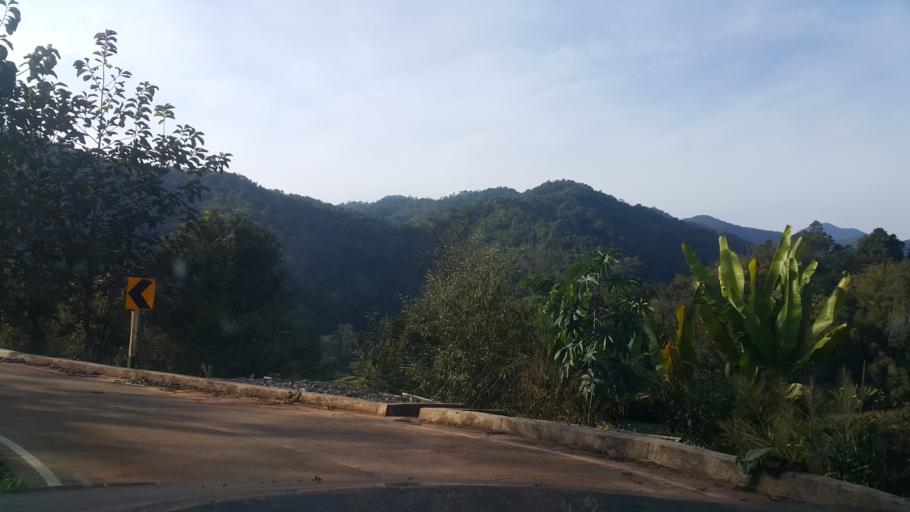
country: TH
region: Chiang Mai
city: Samoeng
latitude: 18.9950
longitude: 98.6760
